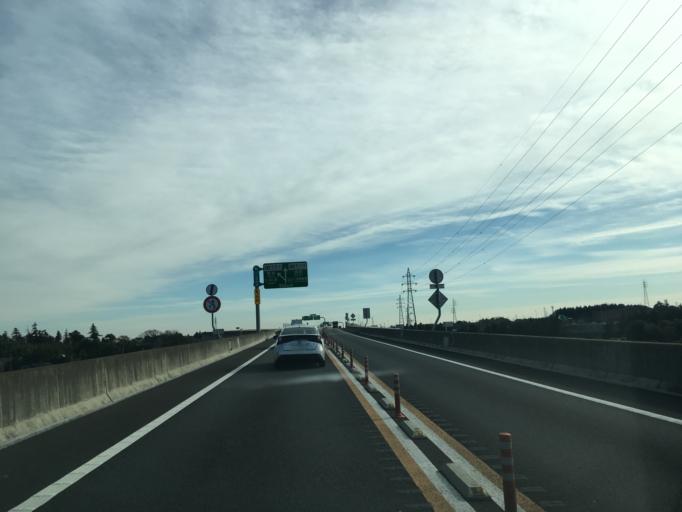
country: JP
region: Ibaraki
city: Naka
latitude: 36.0363
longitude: 140.1188
